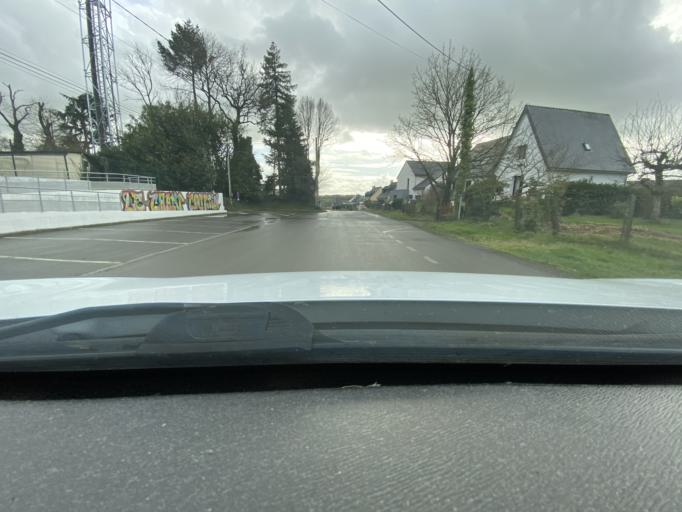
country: FR
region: Brittany
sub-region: Departement d'Ille-et-Vilaine
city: Melesse
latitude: 48.2181
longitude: -1.7086
